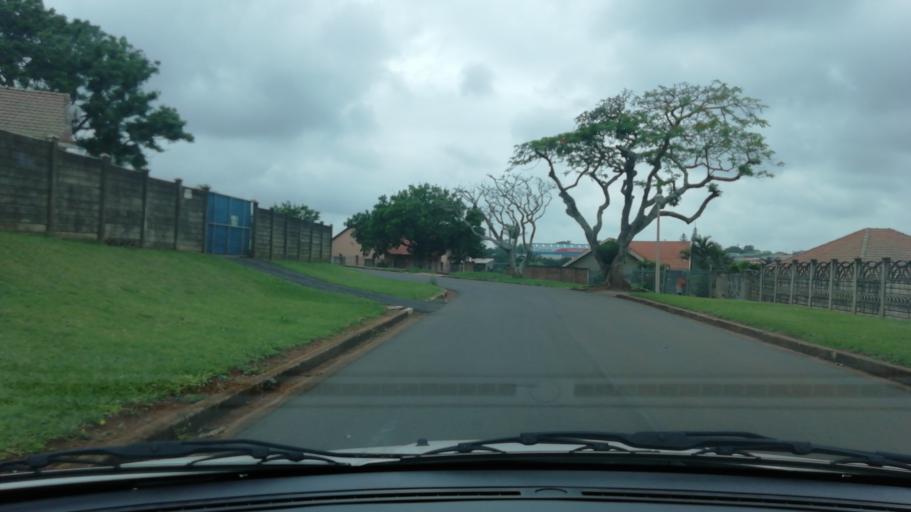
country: ZA
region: KwaZulu-Natal
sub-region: uThungulu District Municipality
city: Empangeni
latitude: -28.7632
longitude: 31.9034
